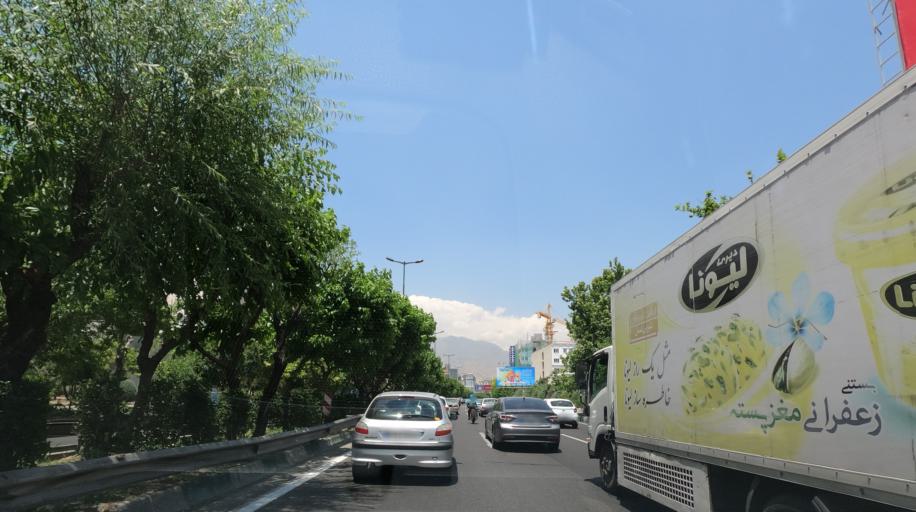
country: IR
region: Tehran
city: Tajrish
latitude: 35.7648
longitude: 51.4217
